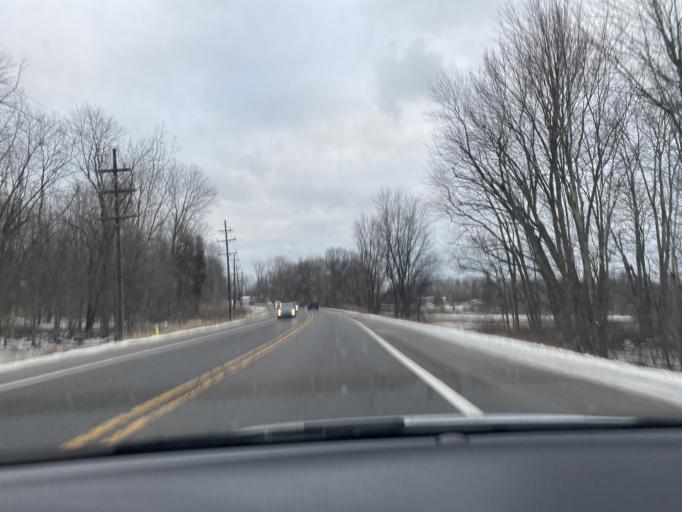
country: US
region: Michigan
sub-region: Lapeer County
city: Imlay City
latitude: 42.9933
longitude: -83.0707
